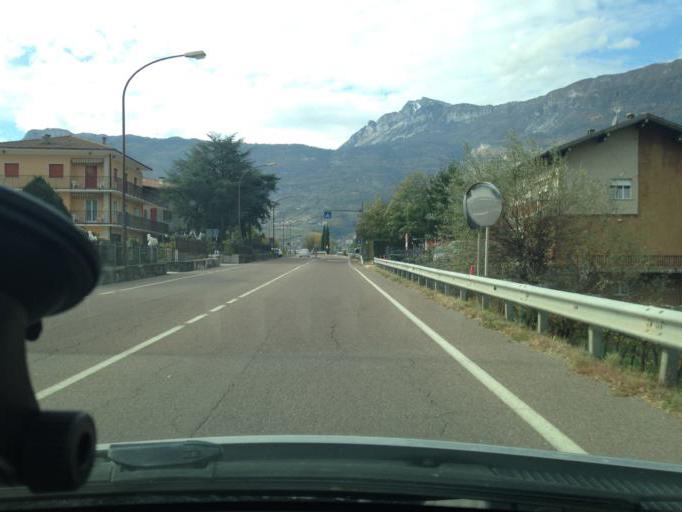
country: IT
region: Trentino-Alto Adige
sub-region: Provincia di Trento
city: Volano
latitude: 45.9172
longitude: 11.0552
